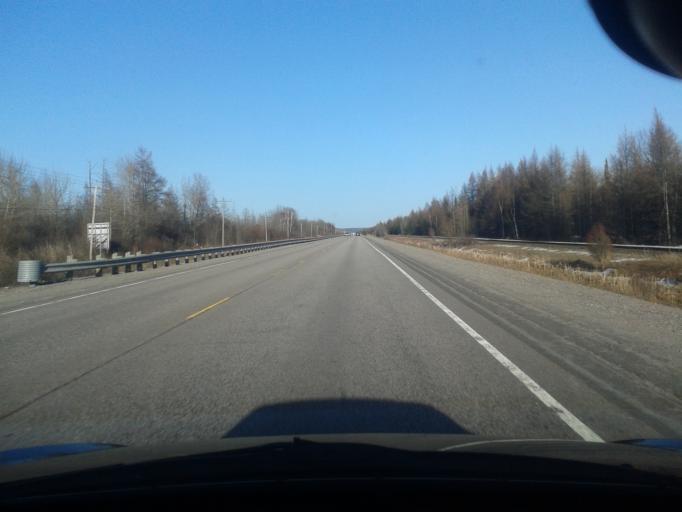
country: CA
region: Ontario
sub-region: Nipissing District
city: North Bay
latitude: 46.3677
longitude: -79.8045
